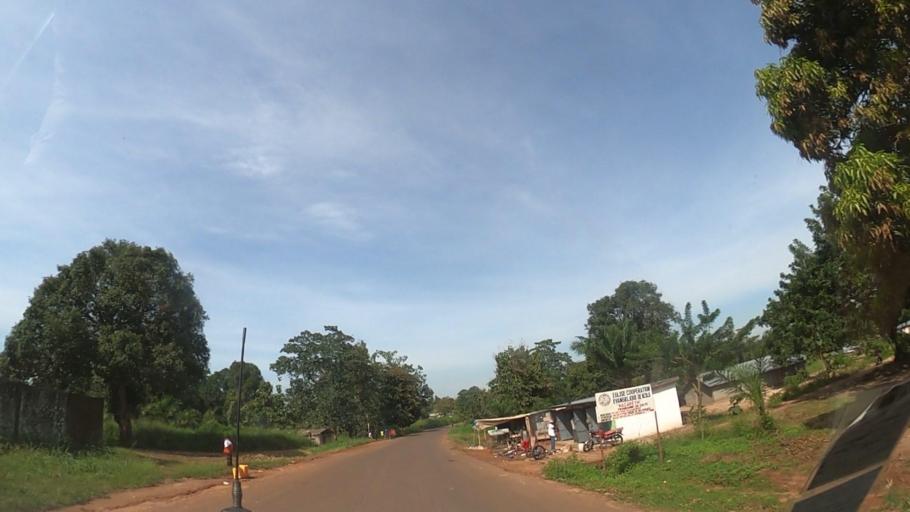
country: CF
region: Bangui
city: Bangui
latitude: 4.3115
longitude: 18.4841
